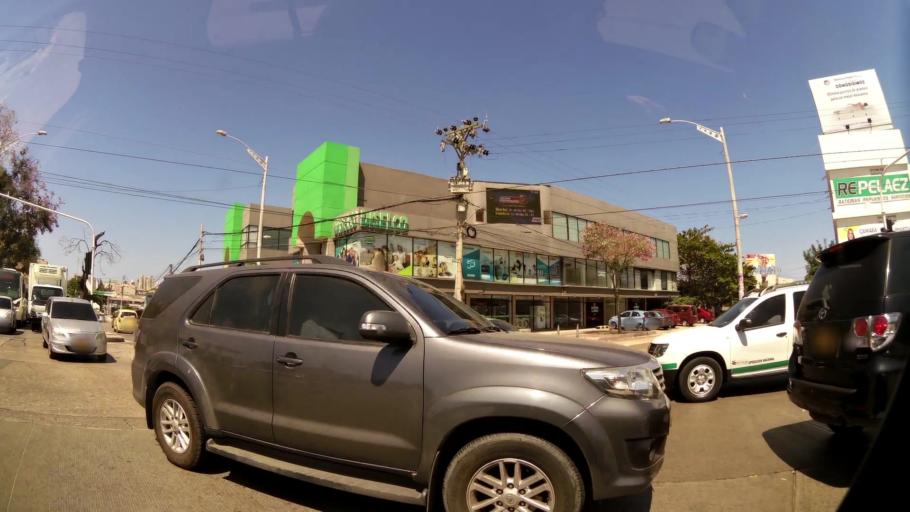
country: CO
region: Atlantico
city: Barranquilla
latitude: 10.9955
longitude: -74.8078
